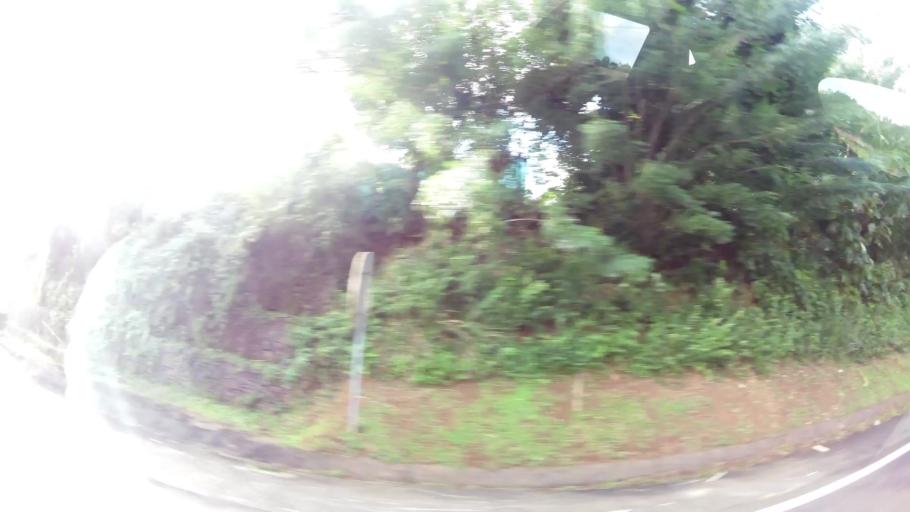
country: MQ
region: Martinique
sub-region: Martinique
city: Ducos
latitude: 14.6015
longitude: -60.9520
